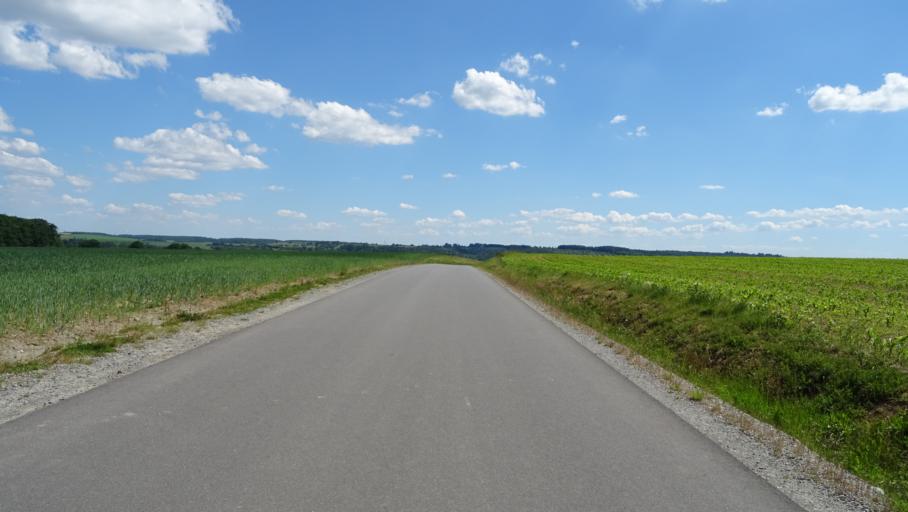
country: DE
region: Baden-Wuerttemberg
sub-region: Karlsruhe Region
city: Adelsheim
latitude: 49.3986
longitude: 9.3679
